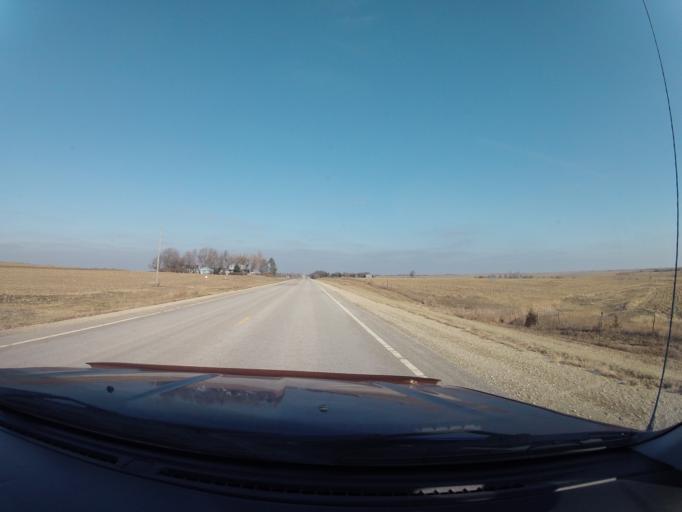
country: US
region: Kansas
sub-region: Marshall County
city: Blue Rapids
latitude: 39.6041
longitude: -96.7501
